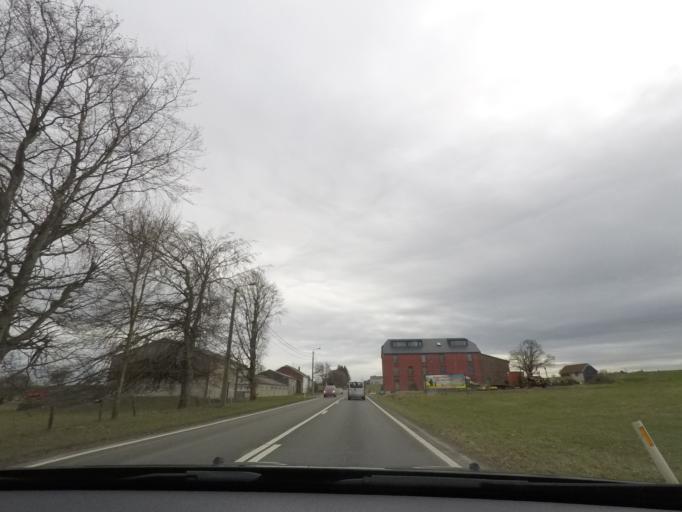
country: BE
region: Wallonia
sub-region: Province du Luxembourg
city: Bastogne
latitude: 49.9927
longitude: 5.7371
